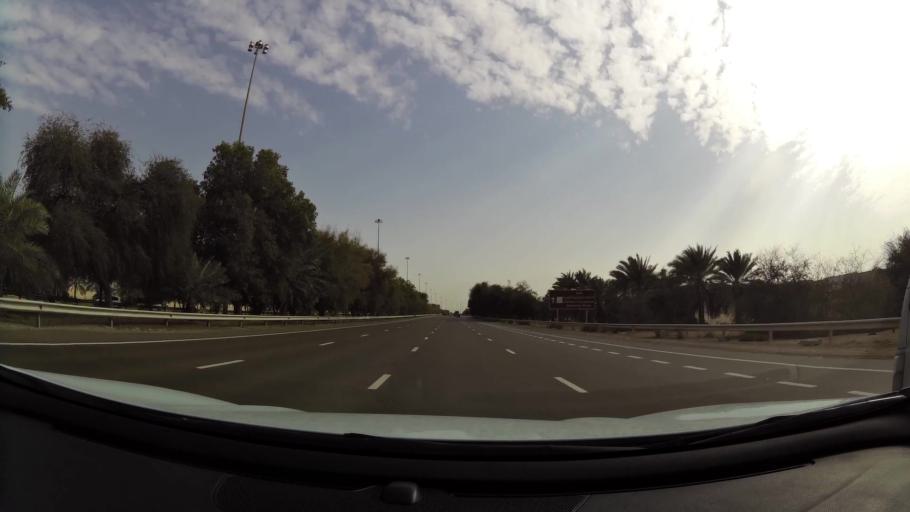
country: AE
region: Abu Dhabi
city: Abu Dhabi
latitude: 24.4580
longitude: 54.6778
